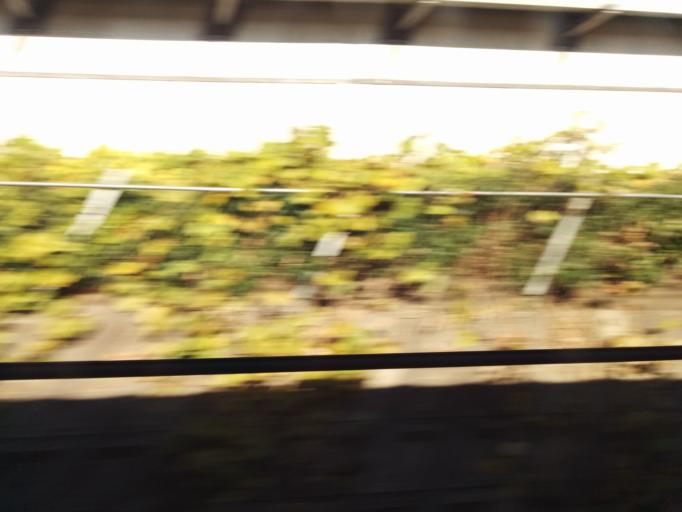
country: JP
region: Kanagawa
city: Yokohama
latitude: 35.4714
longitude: 139.5533
